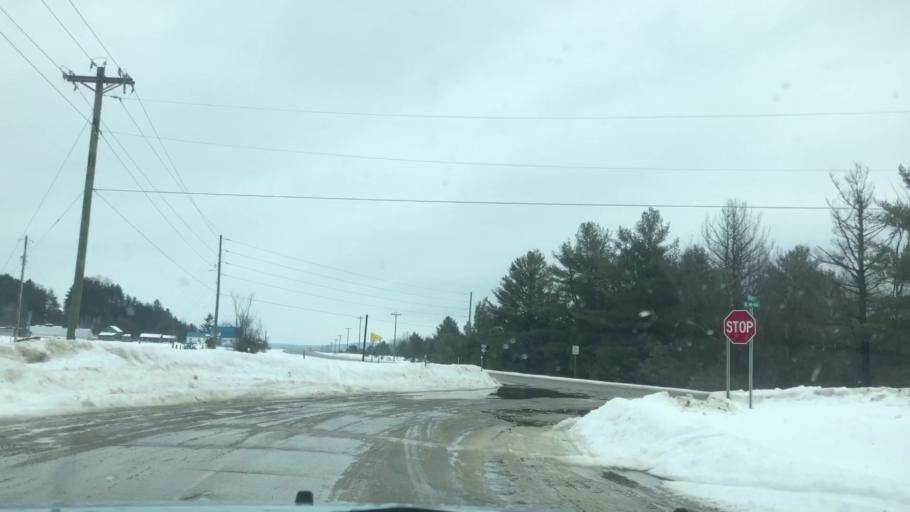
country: US
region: Michigan
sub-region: Charlevoix County
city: East Jordan
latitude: 45.1124
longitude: -85.1294
